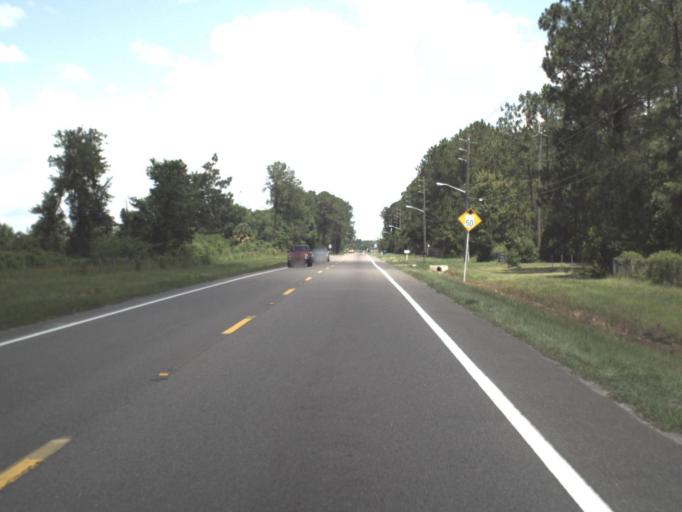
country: US
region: Florida
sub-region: Nassau County
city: Nassau Village-Ratliff
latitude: 30.5029
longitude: -81.7491
